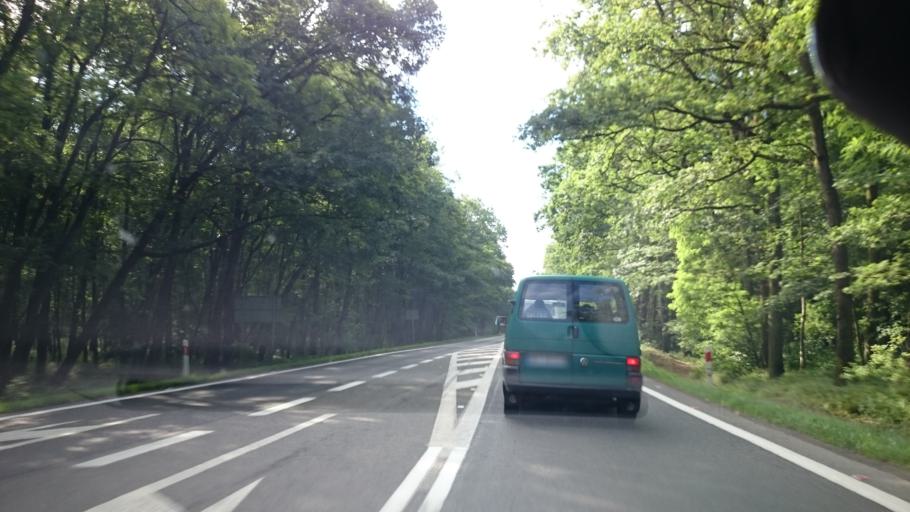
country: PL
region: Opole Voivodeship
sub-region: Powiat opolski
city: Tarnow Opolski
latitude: 50.5948
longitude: 18.0926
